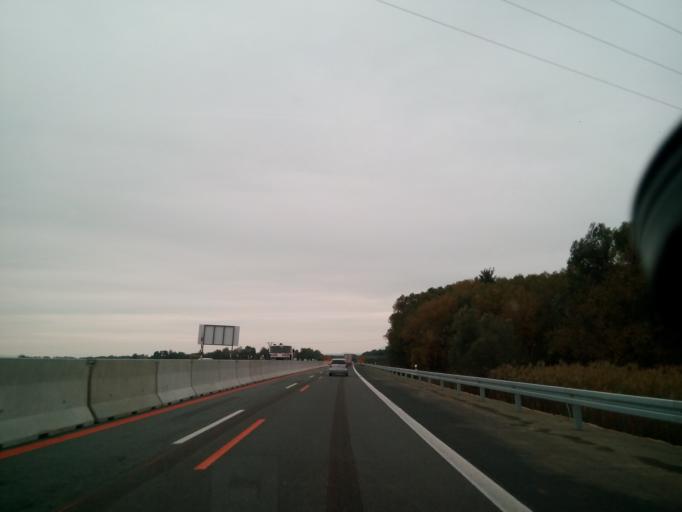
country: SK
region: Kosicky
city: Kosice
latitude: 48.8105
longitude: 21.3095
